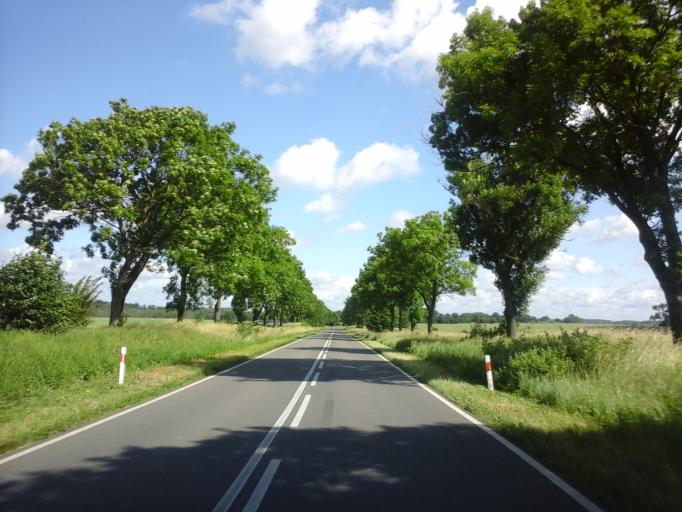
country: PL
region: West Pomeranian Voivodeship
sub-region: Powiat choszczenski
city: Recz
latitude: 53.3073
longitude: 15.5622
